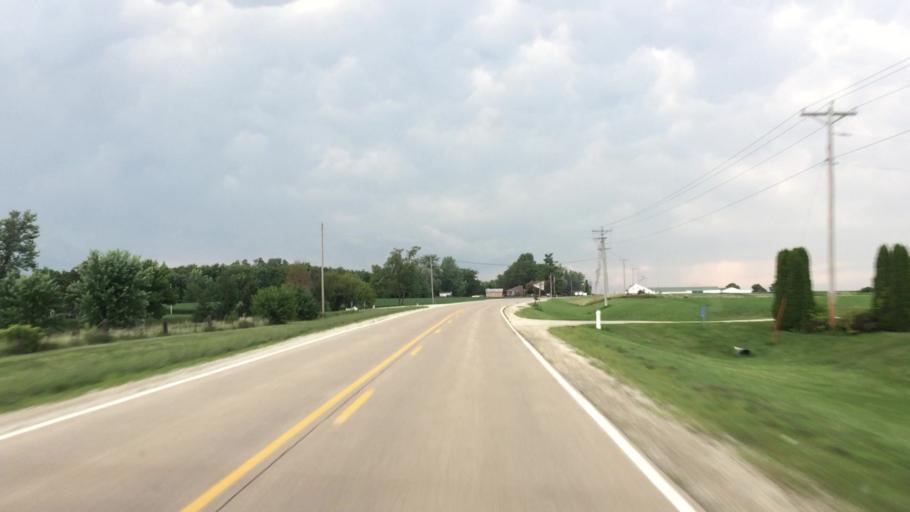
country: US
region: Iowa
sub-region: Lee County
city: Fort Madison
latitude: 40.7310
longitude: -91.3295
